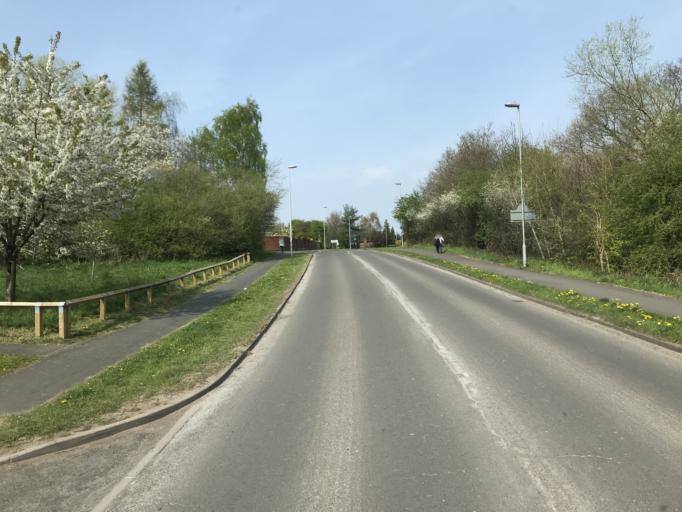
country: GB
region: England
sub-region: Cheshire West and Chester
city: Hoole
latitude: 53.1789
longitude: -2.8598
